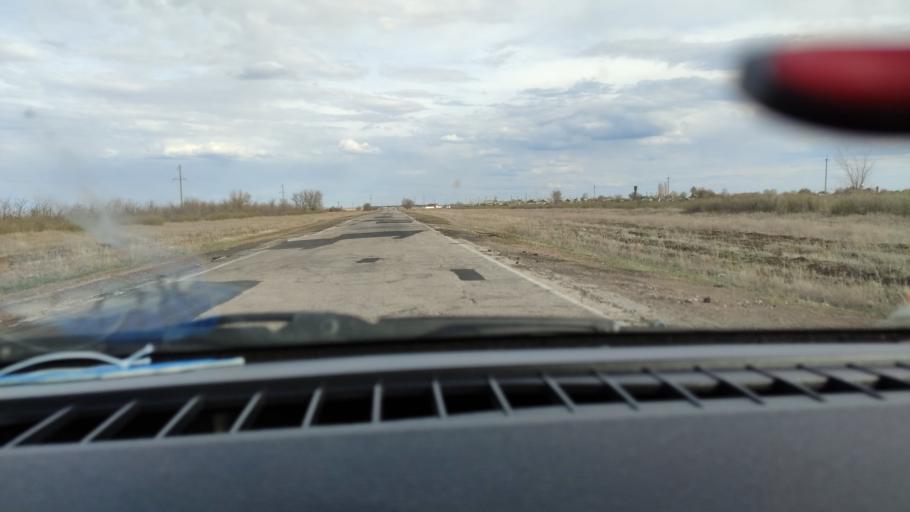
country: RU
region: Saratov
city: Rovnoye
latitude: 51.0626
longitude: 46.0182
